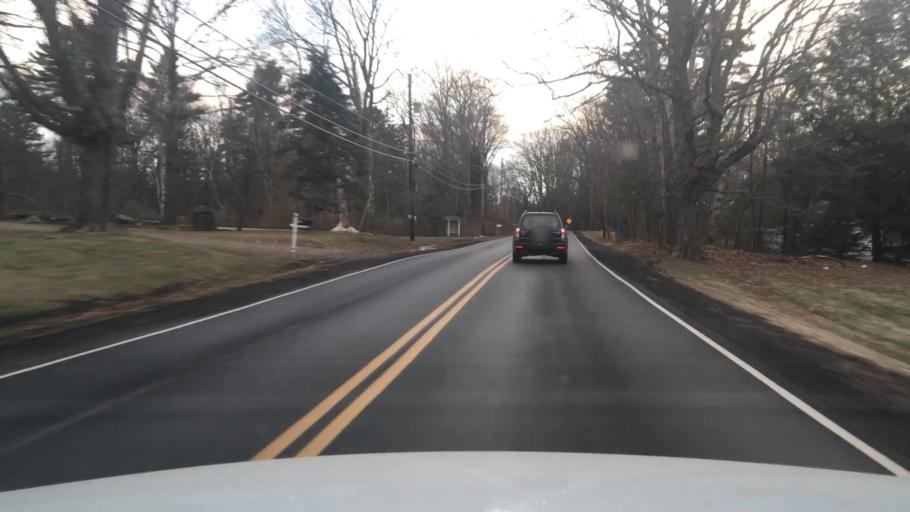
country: US
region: Maine
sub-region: Lincoln County
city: Damariscotta
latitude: 44.0112
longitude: -69.5311
